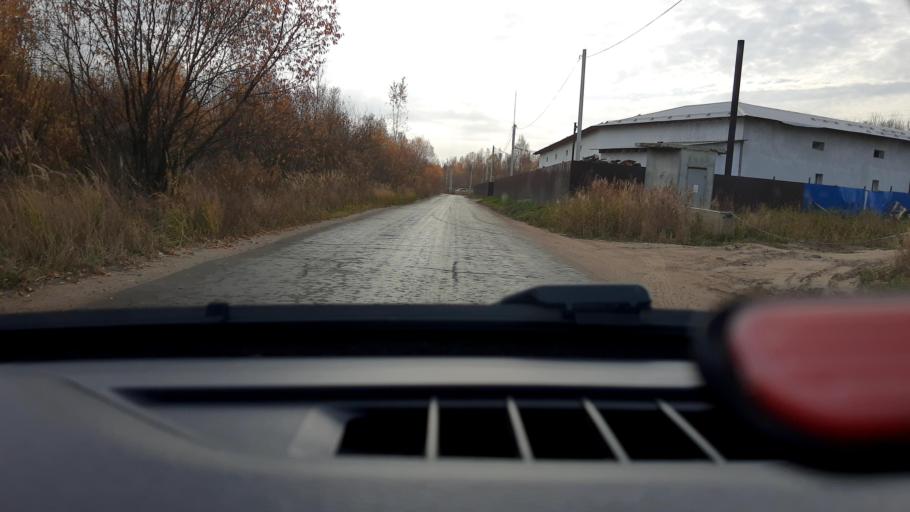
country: RU
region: Nizjnij Novgorod
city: Gorbatovka
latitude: 56.3185
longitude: 43.8465
